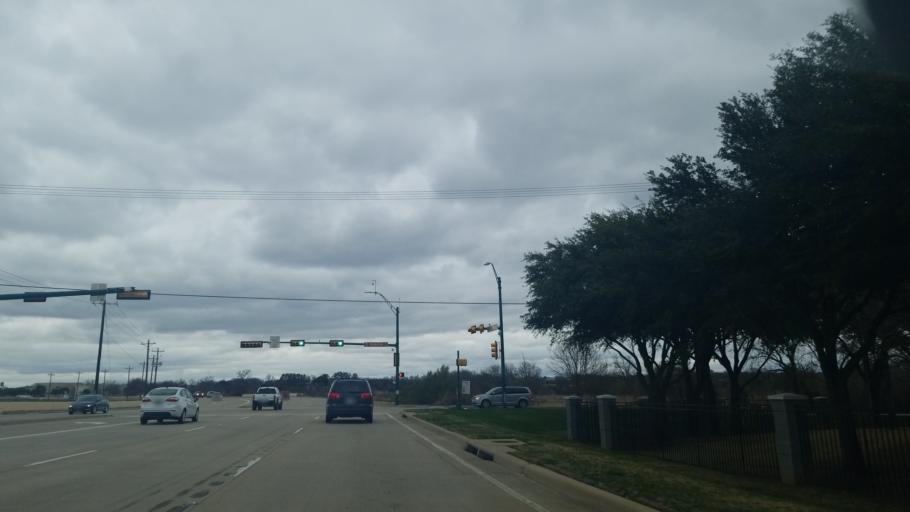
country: US
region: Texas
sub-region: Denton County
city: Double Oak
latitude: 33.0586
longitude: -97.0752
